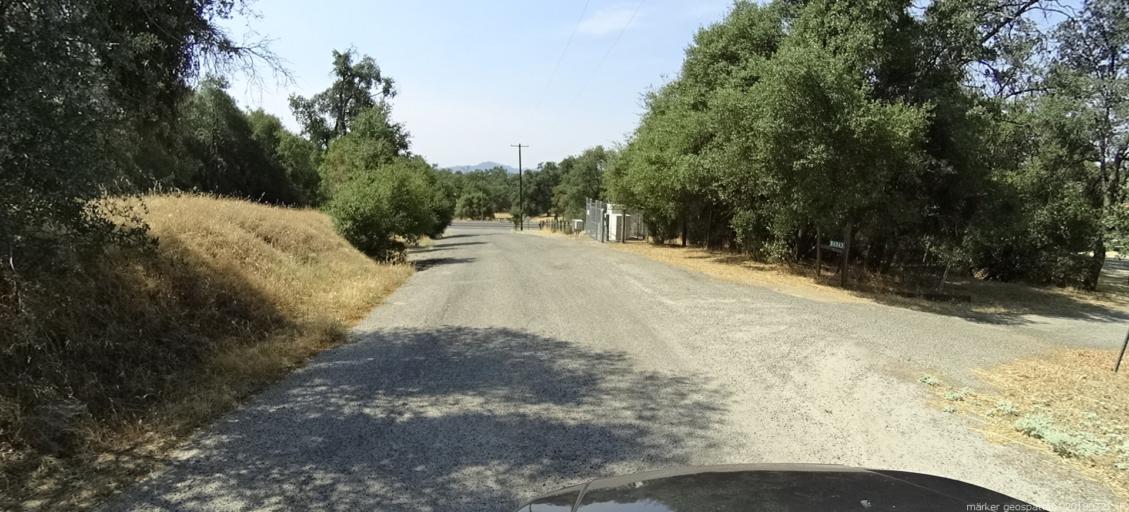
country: US
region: California
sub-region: Fresno County
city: Auberry
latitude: 37.2133
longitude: -119.5215
